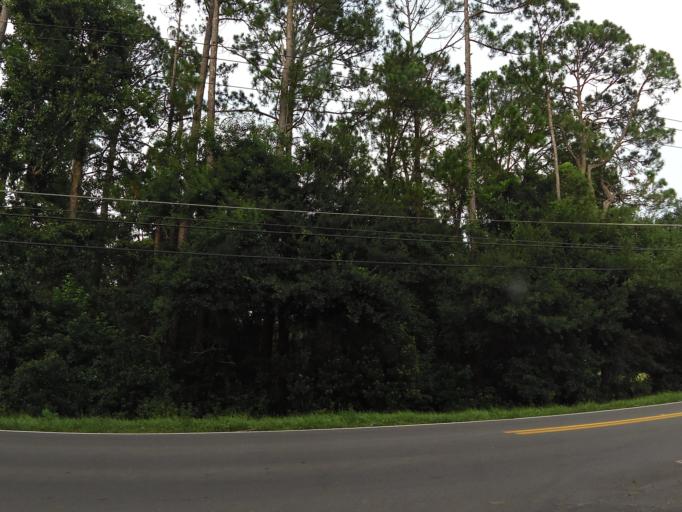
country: US
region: Florida
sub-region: Duval County
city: Jacksonville
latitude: 30.3953
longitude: -81.7524
